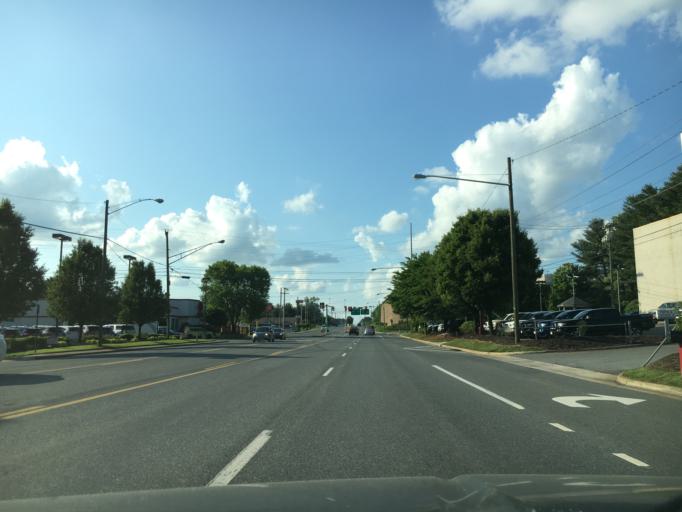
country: US
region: Virginia
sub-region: City of Lynchburg
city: West Lynchburg
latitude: 37.3603
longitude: -79.1809
